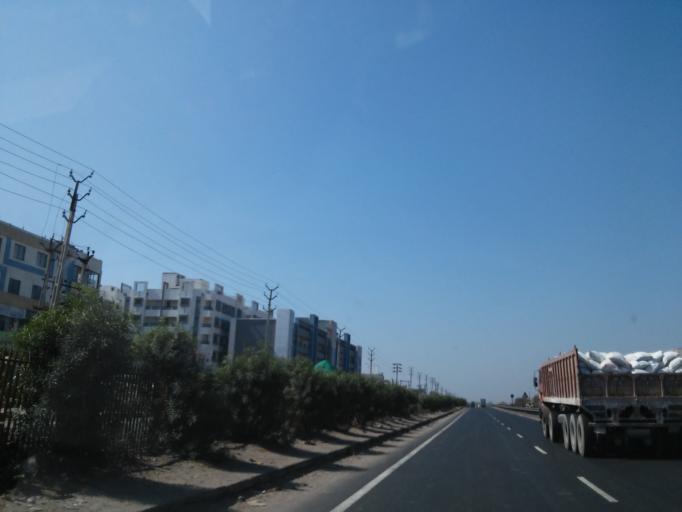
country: IN
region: Gujarat
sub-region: Sabar Kantha
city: Himatnagar
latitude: 23.5811
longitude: 72.9736
